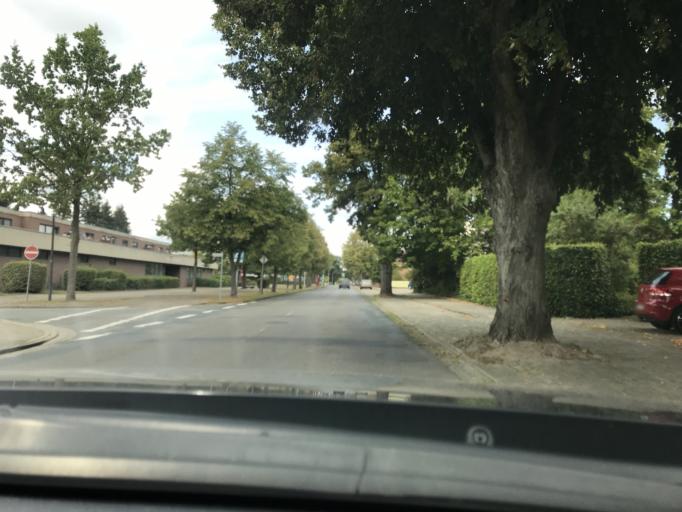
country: DE
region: Lower Saxony
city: Suderburg
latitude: 52.9008
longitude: 10.4387
